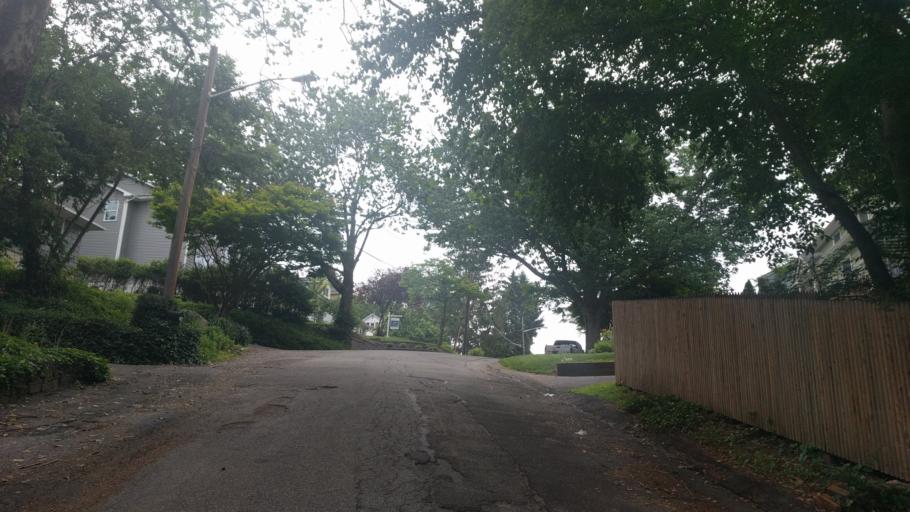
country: US
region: New York
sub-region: Nassau County
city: Glenwood Landing
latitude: 40.8325
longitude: -73.6389
